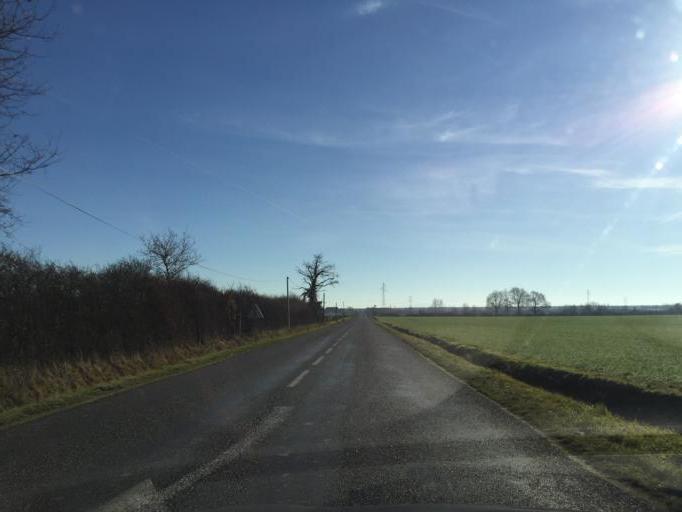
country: FR
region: Auvergne
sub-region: Departement de l'Allier
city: Saint-Pourcain-sur-Sioule
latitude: 46.2645
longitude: 3.2906
